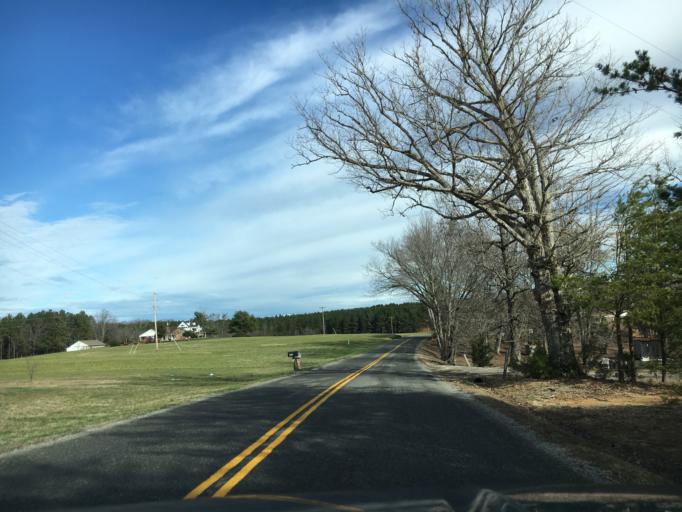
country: US
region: Virginia
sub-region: Nottoway County
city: Crewe
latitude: 37.2863
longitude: -78.2031
